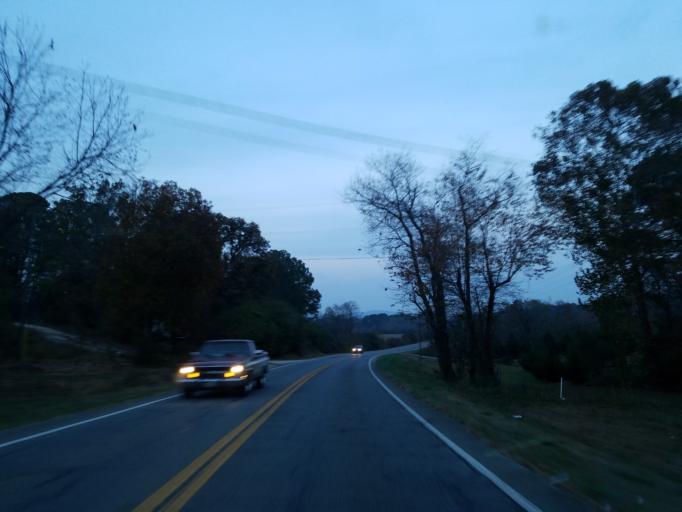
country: US
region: Georgia
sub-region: Pickens County
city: Jasper
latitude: 34.5149
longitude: -84.5431
